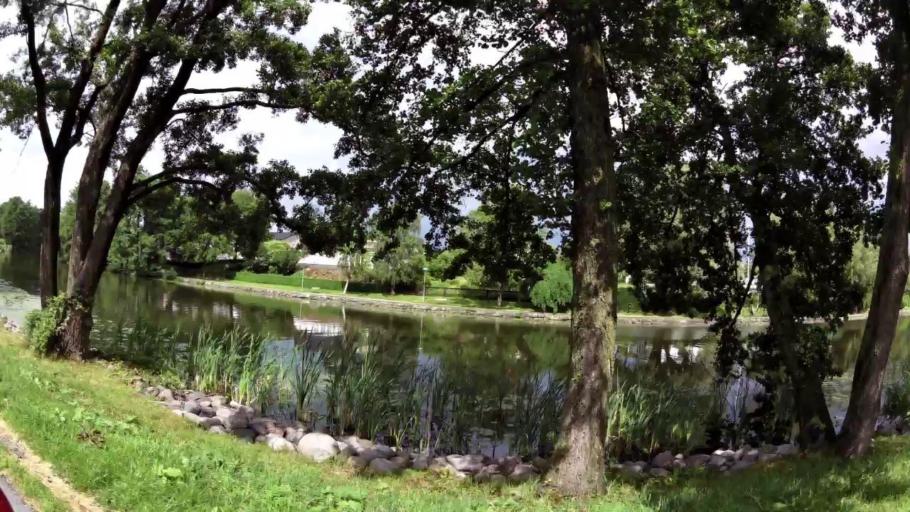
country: SE
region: OEstergoetland
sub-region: Linkopings Kommun
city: Linkoping
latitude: 58.4050
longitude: 15.6364
